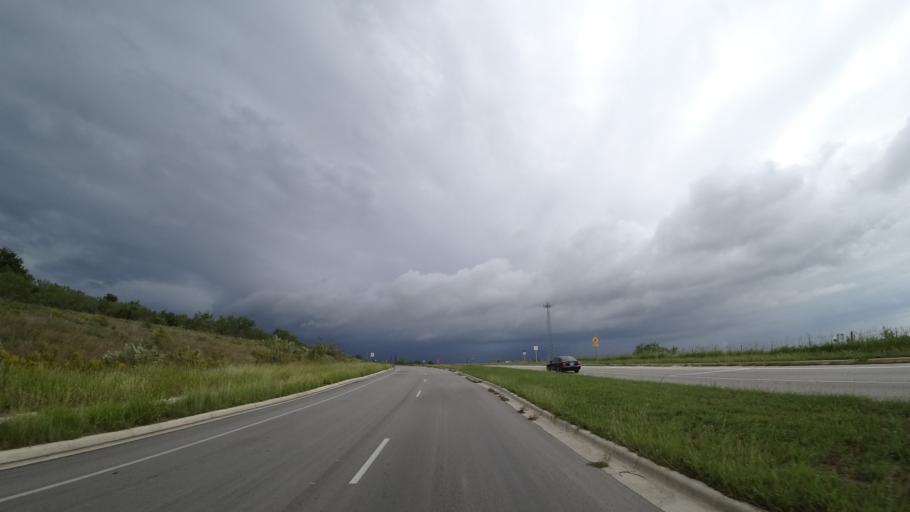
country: US
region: Texas
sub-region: Travis County
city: Onion Creek
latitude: 30.1532
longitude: -97.7317
